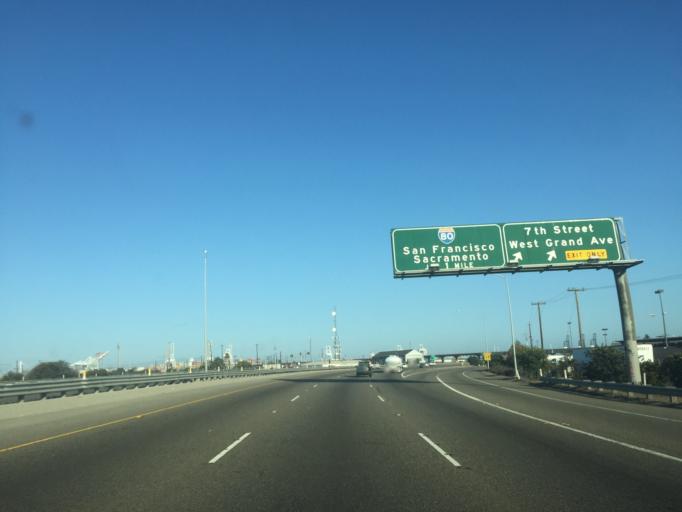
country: US
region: California
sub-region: Alameda County
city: Oakland
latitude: 37.8036
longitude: -122.3016
